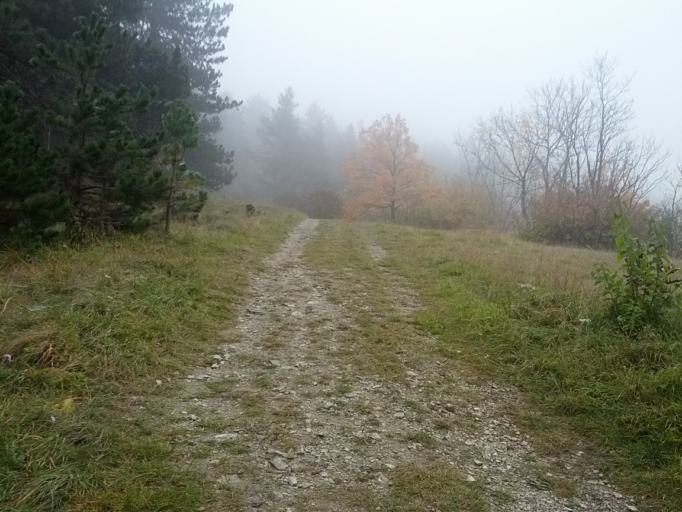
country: DE
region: Thuringia
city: Eisenach
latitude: 50.9747
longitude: 10.3528
